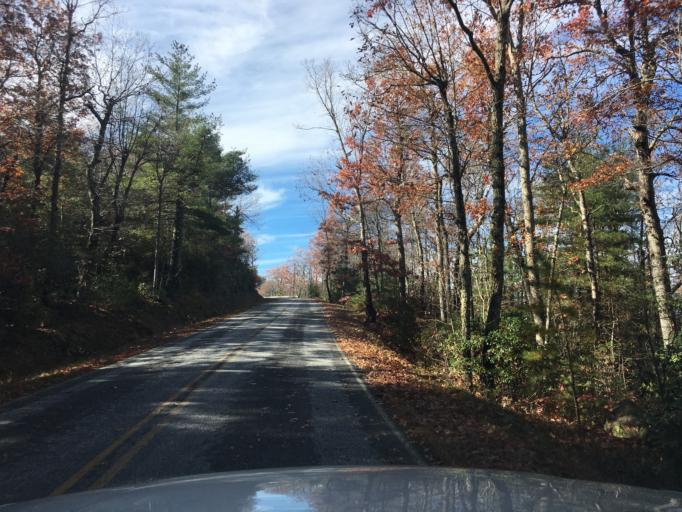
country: US
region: North Carolina
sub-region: Henderson County
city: Valley Hill
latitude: 35.2335
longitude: -82.5186
